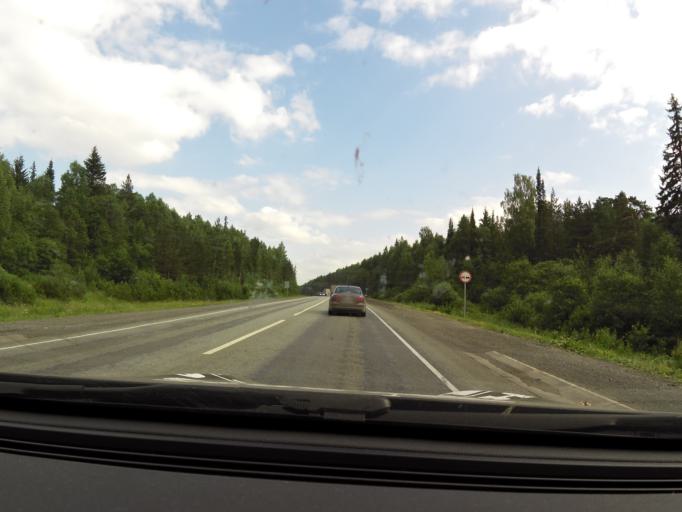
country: RU
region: Sverdlovsk
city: Revda
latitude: 56.8389
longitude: 59.8291
